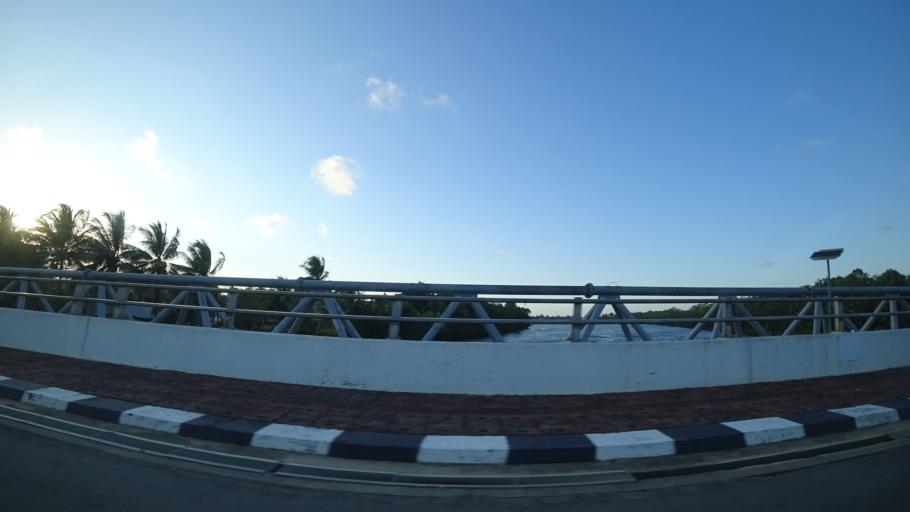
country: BN
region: Tutong
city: Tutong
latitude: 4.7973
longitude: 114.6462
